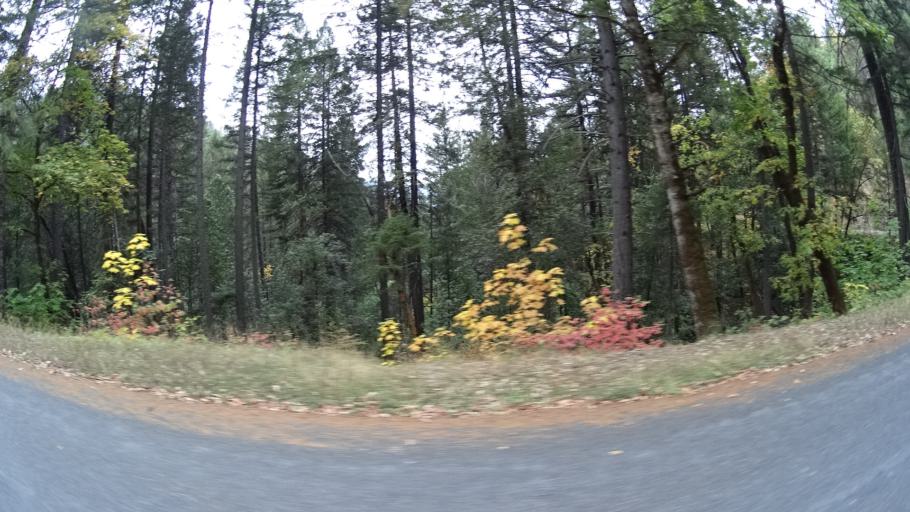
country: US
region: California
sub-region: Siskiyou County
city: Happy Camp
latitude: 41.7607
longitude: -123.3623
